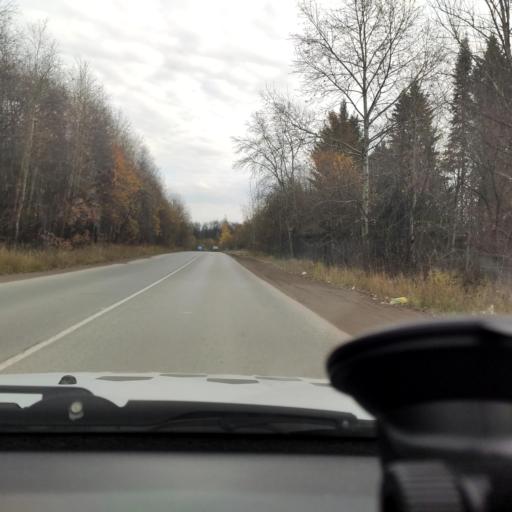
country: RU
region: Perm
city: Froly
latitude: 57.9558
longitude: 56.2968
